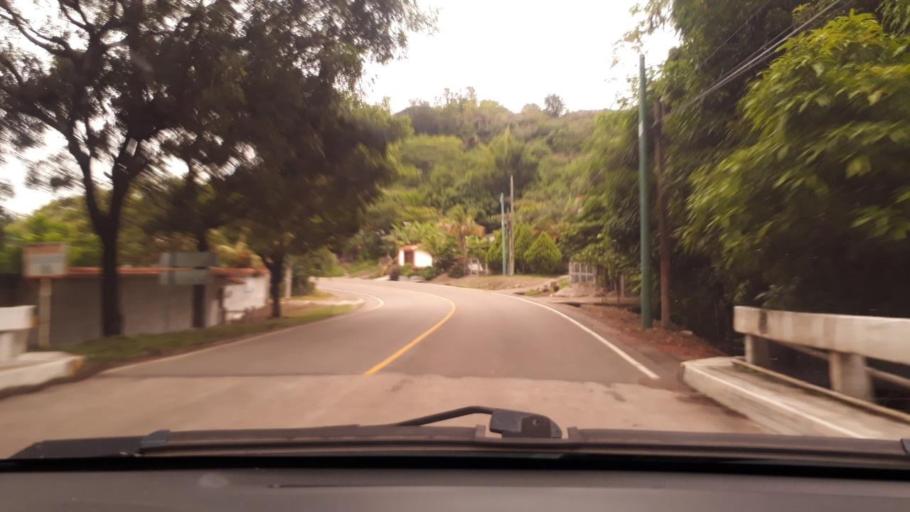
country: GT
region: Chiquimula
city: Concepcion Las Minas
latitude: 14.5182
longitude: -89.4683
